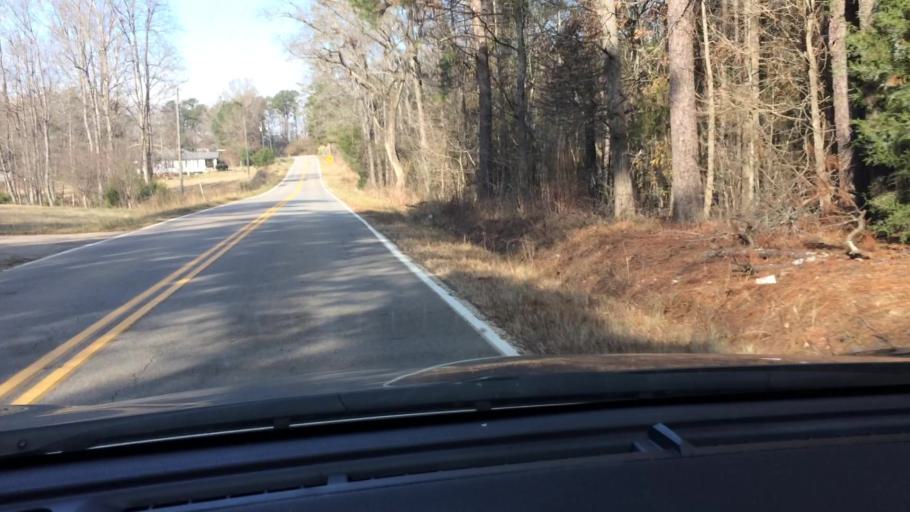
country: US
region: South Carolina
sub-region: Newberry County
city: Newberry
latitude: 34.2604
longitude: -81.5685
